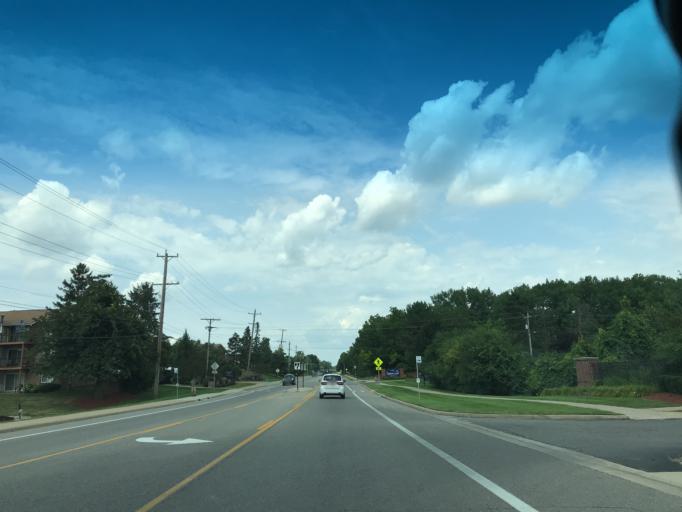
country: US
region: Michigan
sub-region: Washtenaw County
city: Ypsilanti
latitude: 42.2530
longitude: -83.6611
